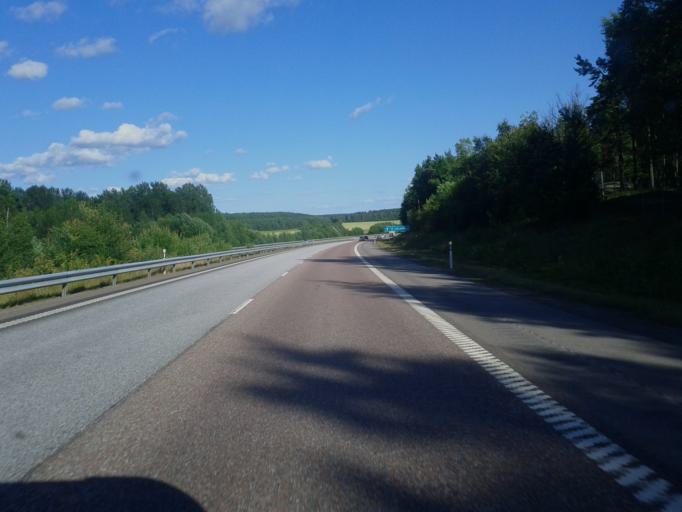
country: SE
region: Uppsala
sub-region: Habo Kommun
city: Balsta
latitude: 59.5916
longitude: 17.4904
